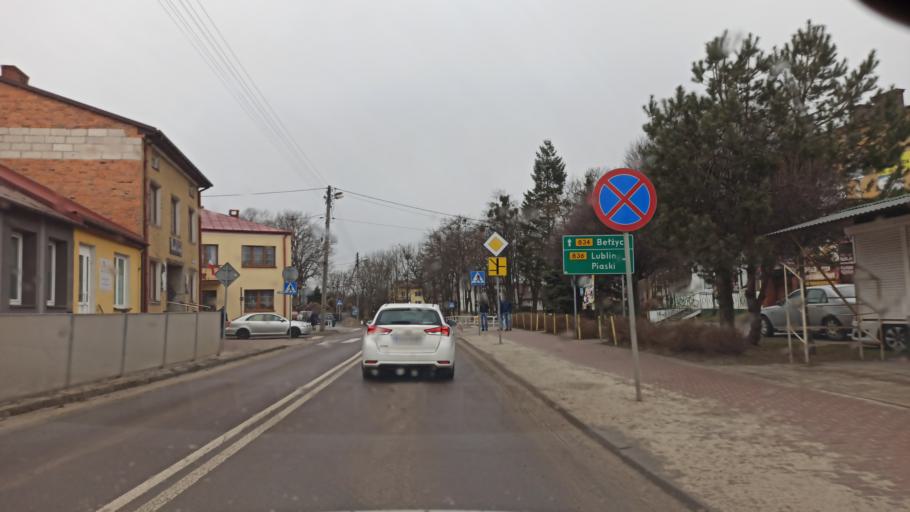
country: PL
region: Lublin Voivodeship
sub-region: Powiat lubelski
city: Bychawa
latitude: 51.0157
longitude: 22.5336
